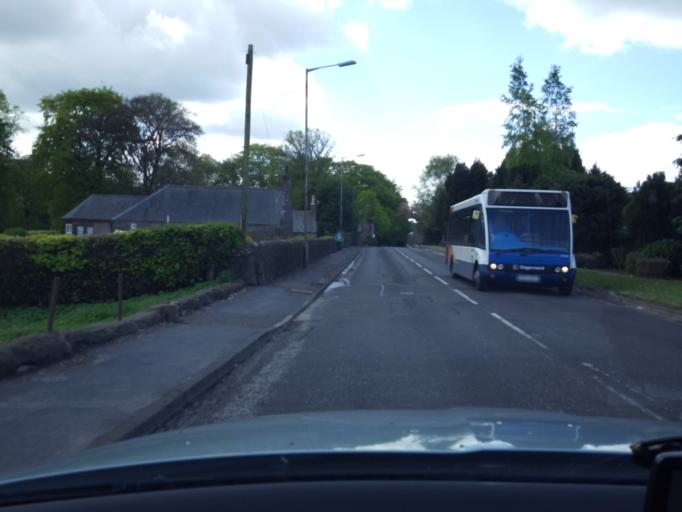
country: GB
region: Scotland
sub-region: Angus
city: Brechin
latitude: 56.7388
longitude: -2.6561
